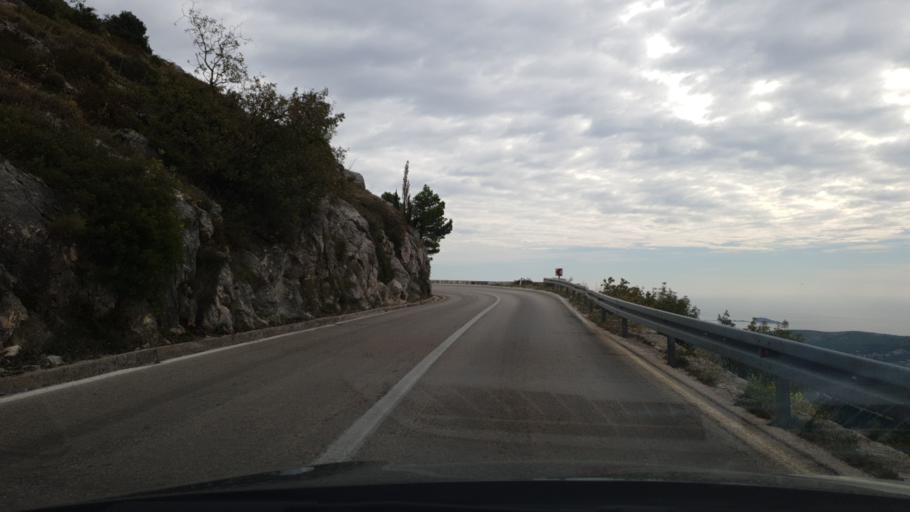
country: HR
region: Dubrovacko-Neretvanska
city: Cibaca
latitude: 42.6587
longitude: 18.1718
